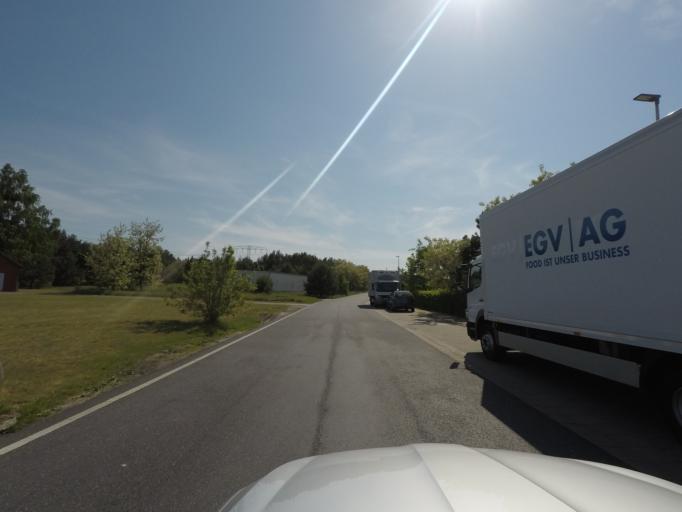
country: DE
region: Brandenburg
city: Britz
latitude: 52.8559
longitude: 13.7684
